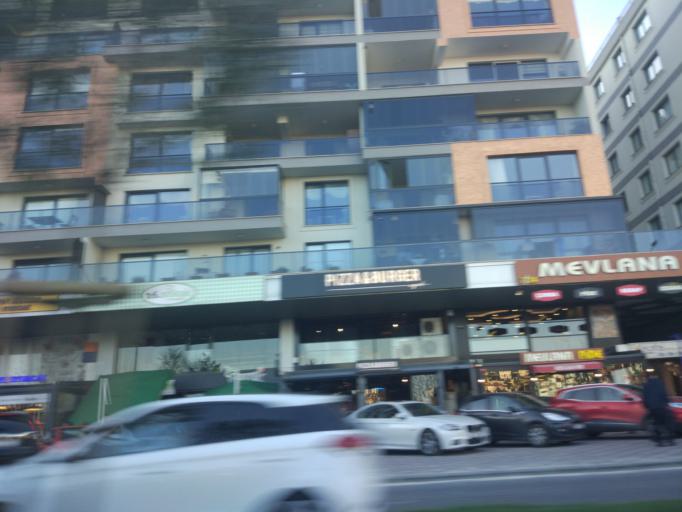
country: TR
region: Istanbul
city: Esenyurt
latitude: 41.0720
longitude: 28.6893
